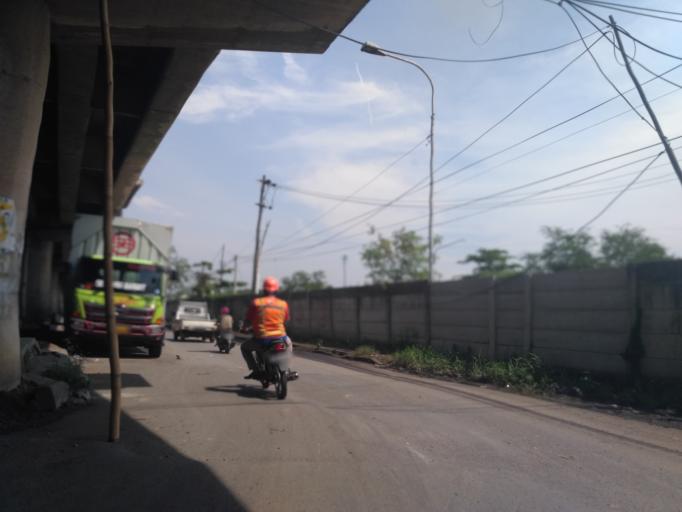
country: ID
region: Central Java
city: Semarang
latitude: -6.9551
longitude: 110.4285
